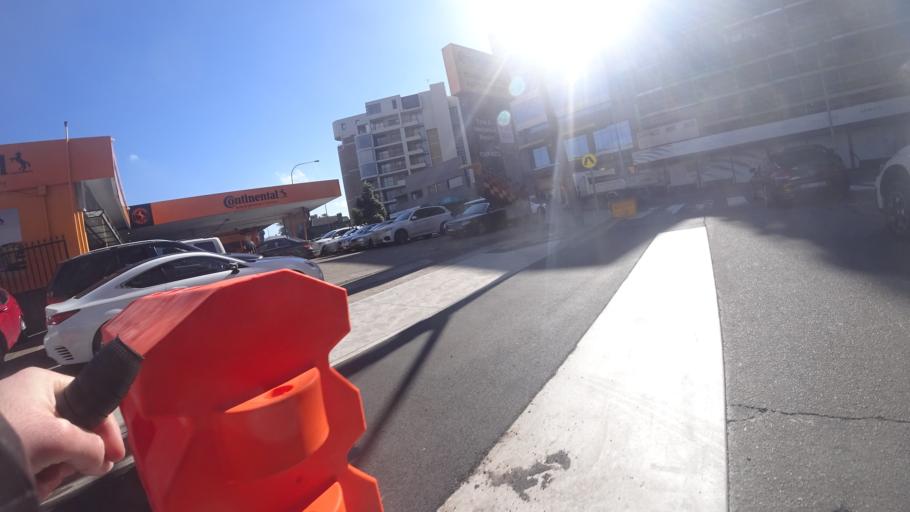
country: AU
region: New South Wales
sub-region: Waverley
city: Bondi Junction
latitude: -33.8914
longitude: 151.2450
